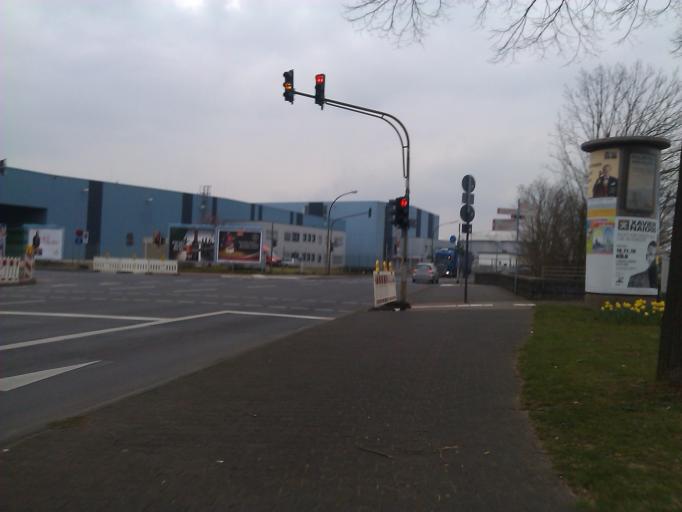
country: DE
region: North Rhine-Westphalia
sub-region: Regierungsbezirk Koln
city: Nippes
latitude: 50.9962
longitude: 6.9604
